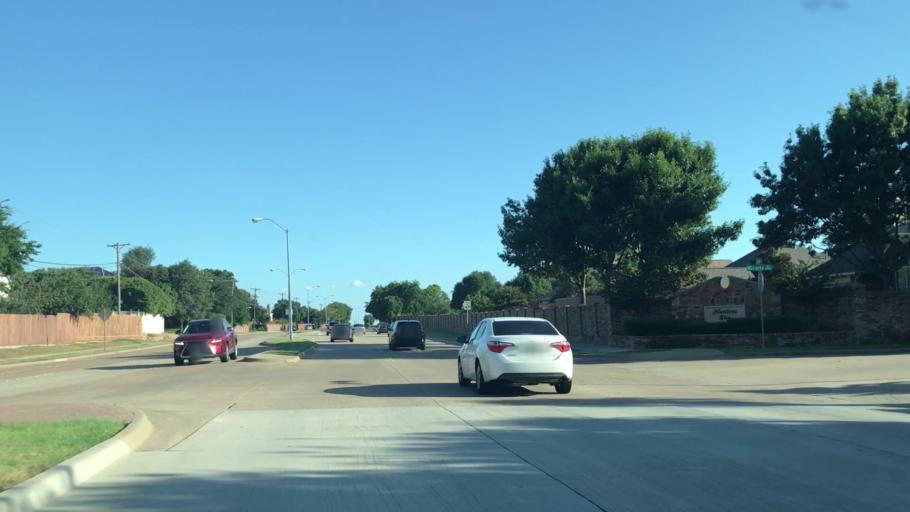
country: US
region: Texas
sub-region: Collin County
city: Plano
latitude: 33.0787
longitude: -96.7368
